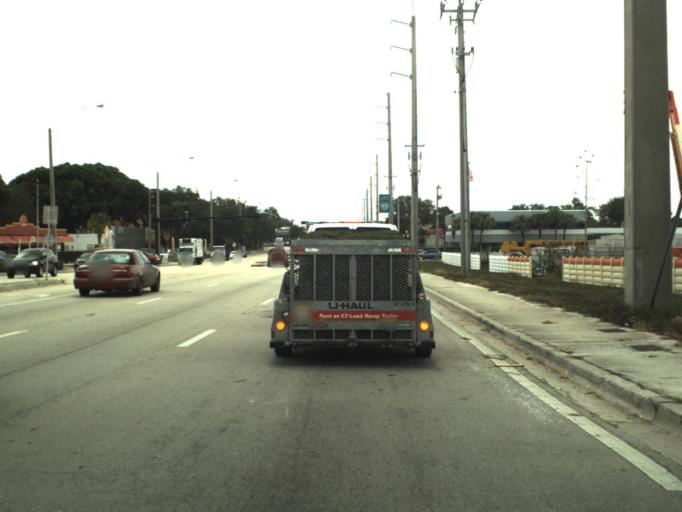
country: US
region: Florida
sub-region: Broward County
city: Dania Beach
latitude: 26.0478
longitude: -80.1676
